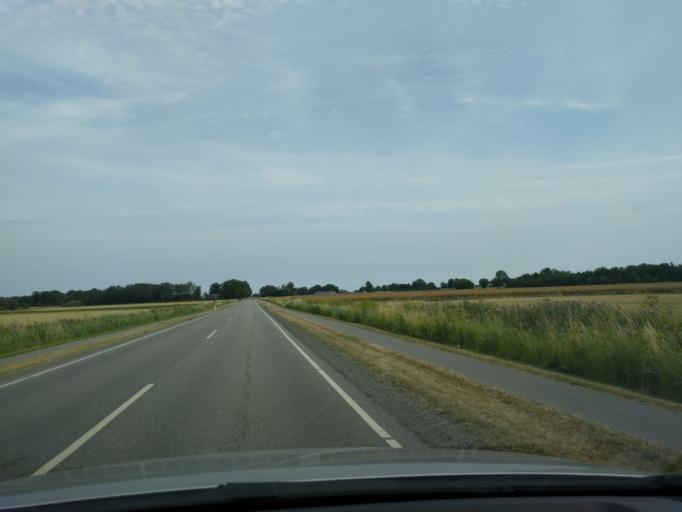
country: DK
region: South Denmark
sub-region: Nordfyns Kommune
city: Otterup
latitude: 55.5431
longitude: 10.4349
